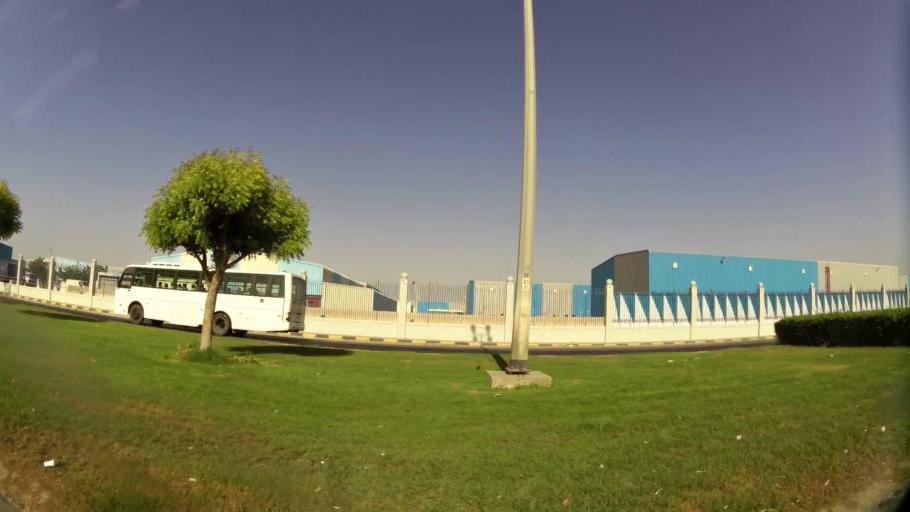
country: AE
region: Ajman
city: Ajman
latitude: 25.4116
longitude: 55.4522
